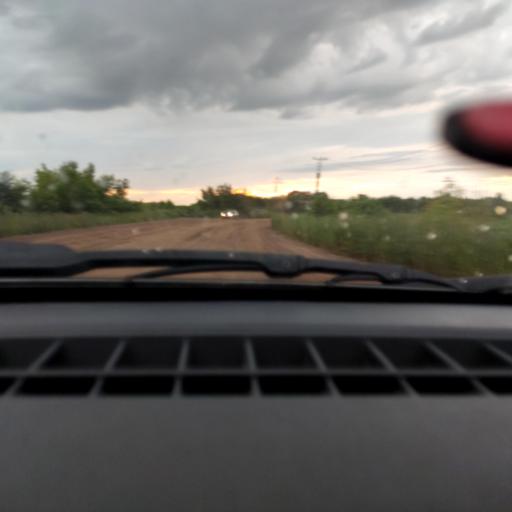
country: RU
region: Bashkortostan
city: Blagoveshchensk
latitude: 54.9201
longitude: 55.9752
